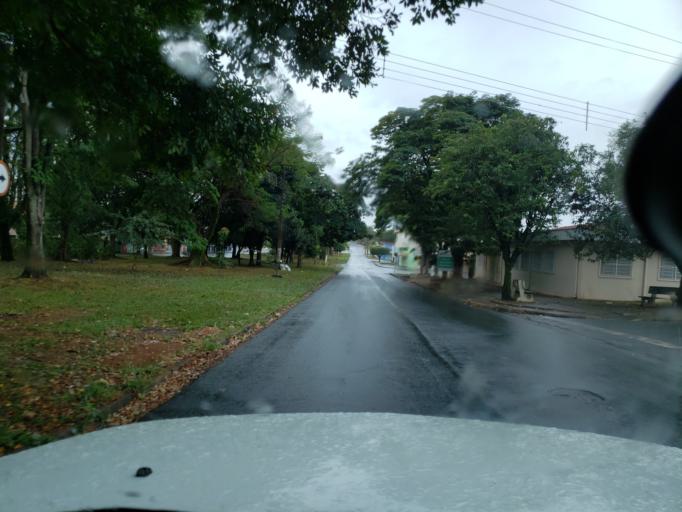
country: BR
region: Sao Paulo
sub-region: Moji-Guacu
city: Mogi-Gaucu
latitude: -22.3500
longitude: -46.9404
